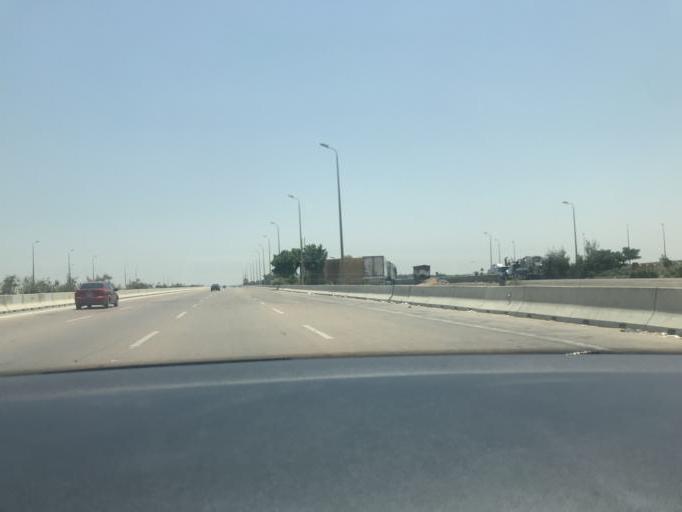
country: EG
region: Al Buhayrah
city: Abu al Matamir
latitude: 30.7296
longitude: 30.0181
